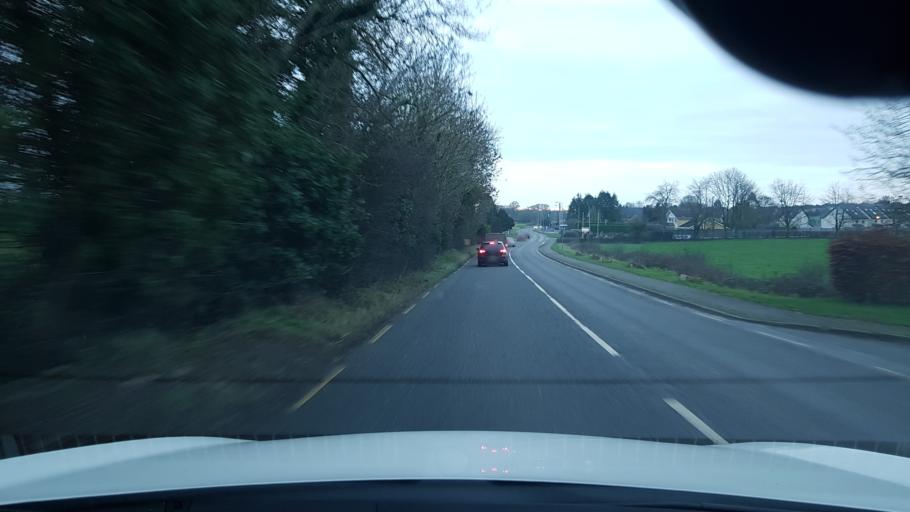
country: IE
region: Leinster
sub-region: An Mhi
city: Navan
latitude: 53.6755
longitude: -6.6764
